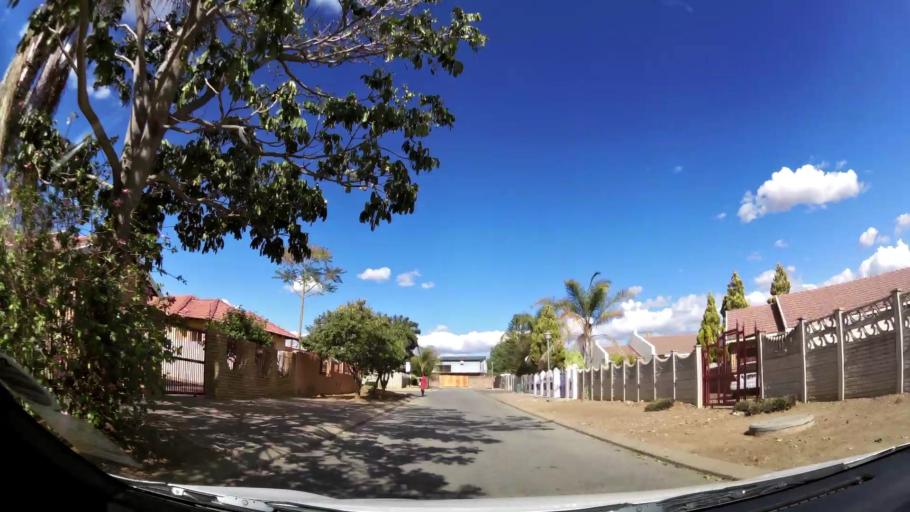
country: ZA
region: Limpopo
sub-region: Capricorn District Municipality
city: Polokwane
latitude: -23.8858
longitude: 29.4720
